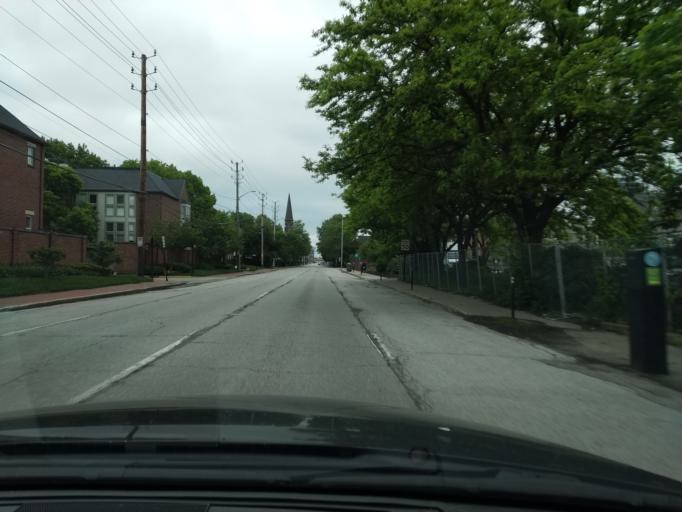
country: US
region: Indiana
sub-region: Marion County
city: Indianapolis
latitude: 39.7736
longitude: -86.1488
